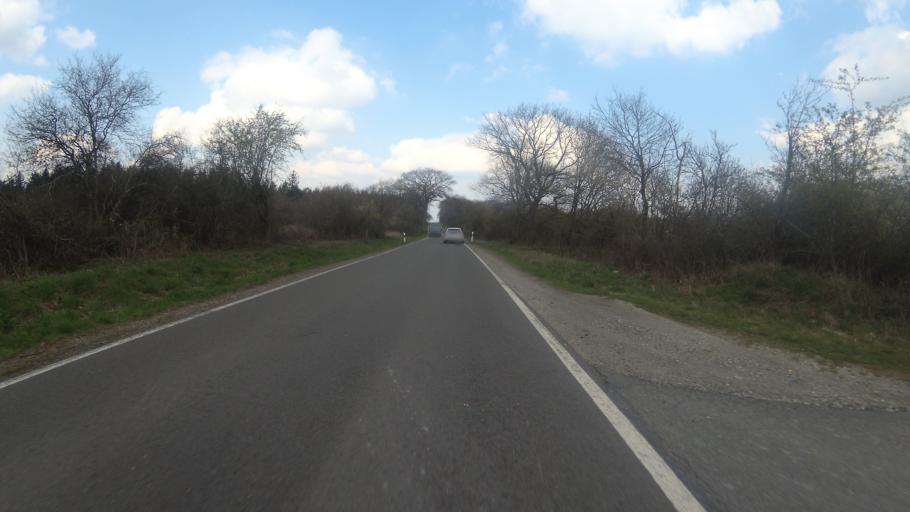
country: DE
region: Rheinland-Pfalz
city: Polich
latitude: 49.7727
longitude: 6.8469
